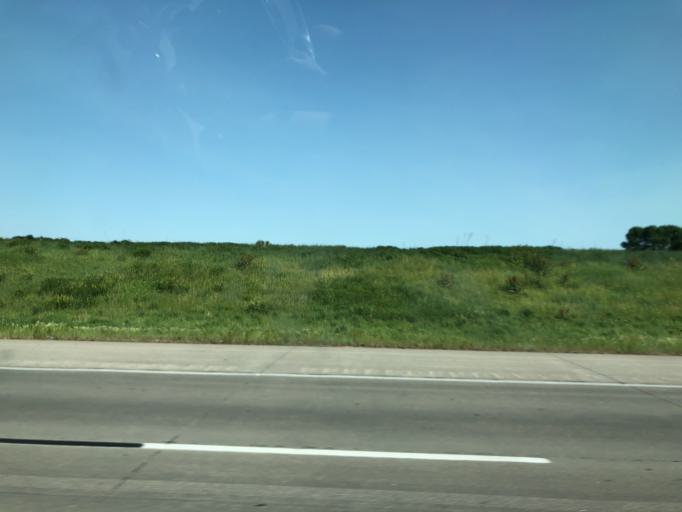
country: US
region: Nebraska
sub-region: Lancaster County
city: Waverly
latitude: 40.9452
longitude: -96.4241
